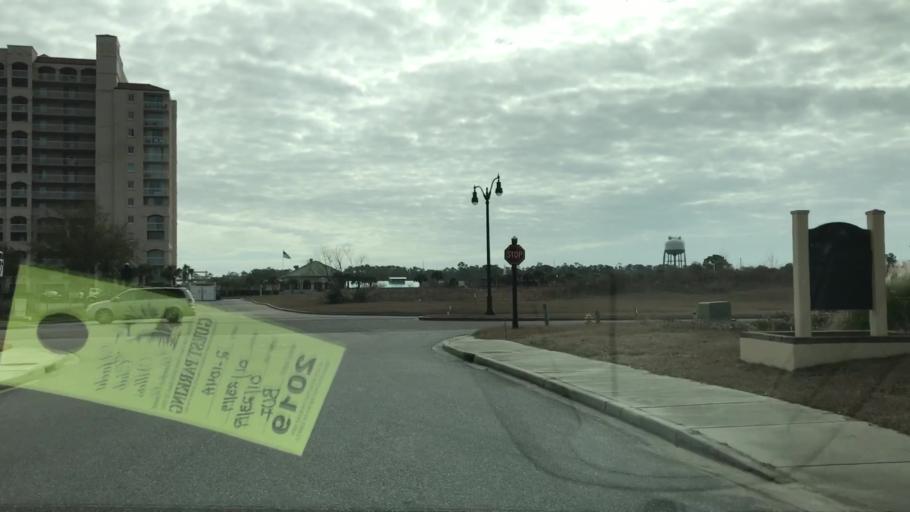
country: US
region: South Carolina
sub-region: Horry County
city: North Myrtle Beach
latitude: 33.8048
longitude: -78.7475
